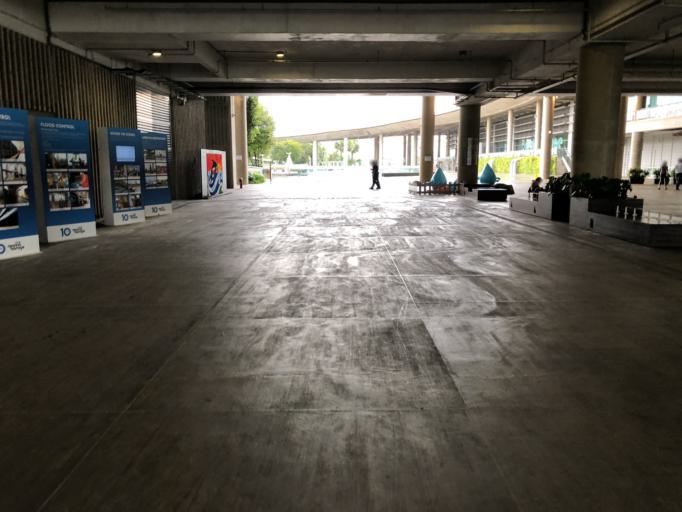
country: SG
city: Singapore
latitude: 1.2799
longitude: 103.8712
